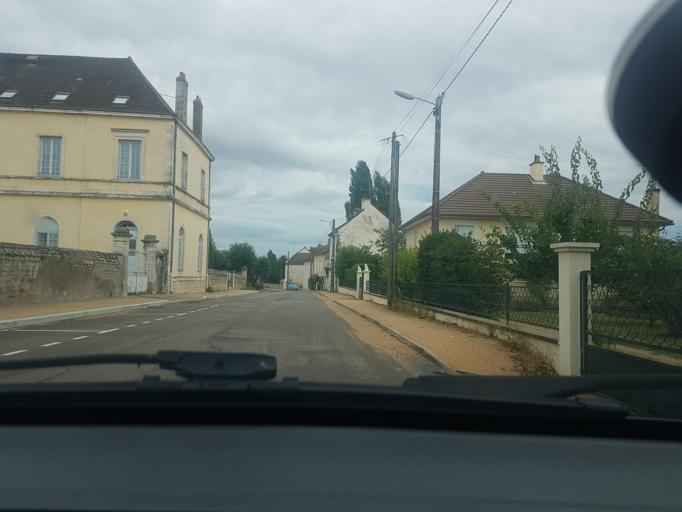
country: FR
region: Bourgogne
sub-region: Departement de Saone-et-Loire
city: Fontaines
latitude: 46.8521
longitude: 4.7689
